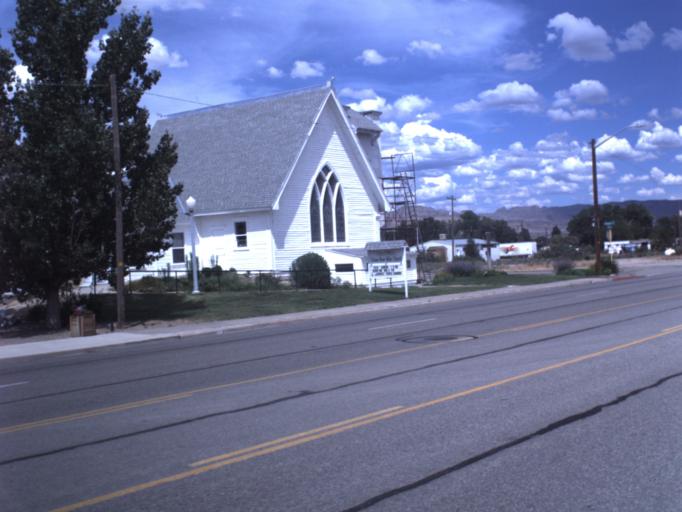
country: US
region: Utah
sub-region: Carbon County
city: East Carbon City
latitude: 38.9954
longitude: -110.1672
